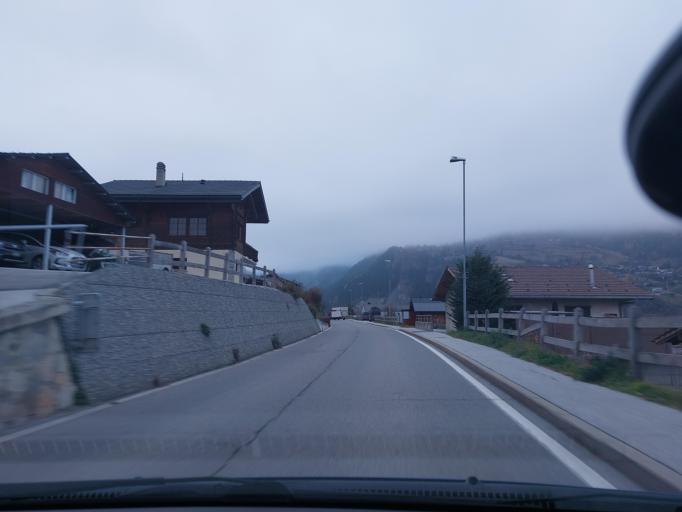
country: CH
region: Valais
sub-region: Herens District
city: Ayent
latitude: 46.2859
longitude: 7.4221
